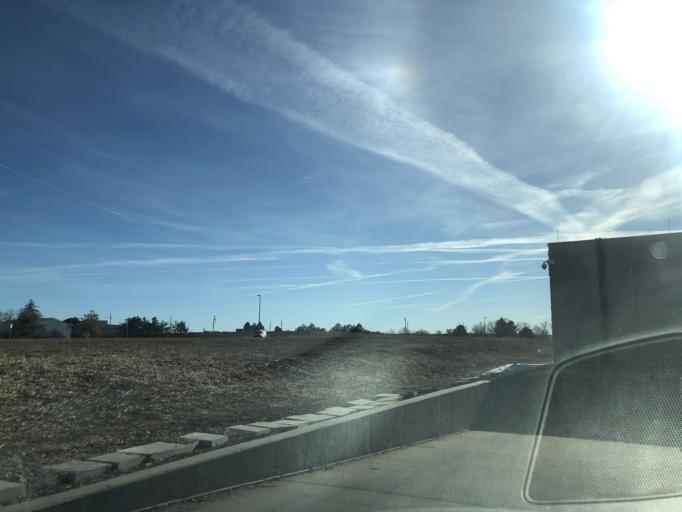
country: US
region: Colorado
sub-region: Adams County
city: Aurora
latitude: 39.7205
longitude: -104.8016
